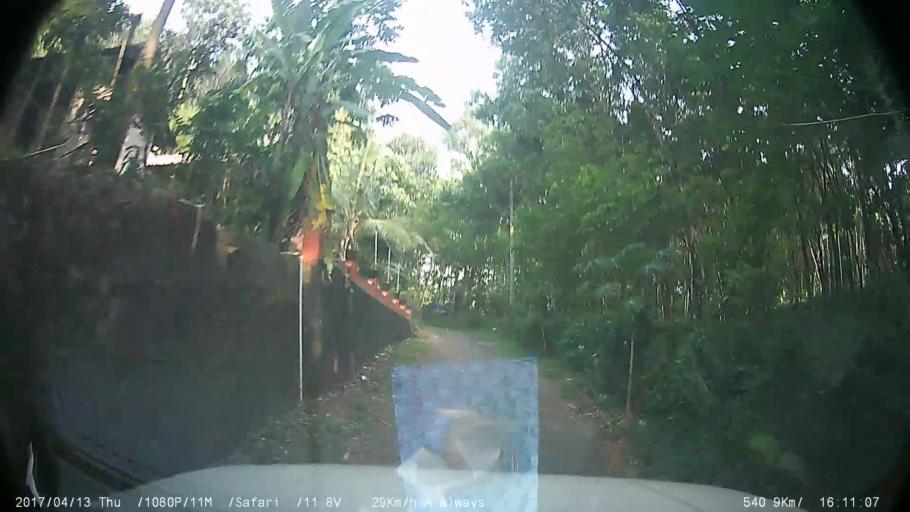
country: IN
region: Kerala
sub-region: Ernakulam
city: Piravam
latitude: 9.8224
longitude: 76.5191
